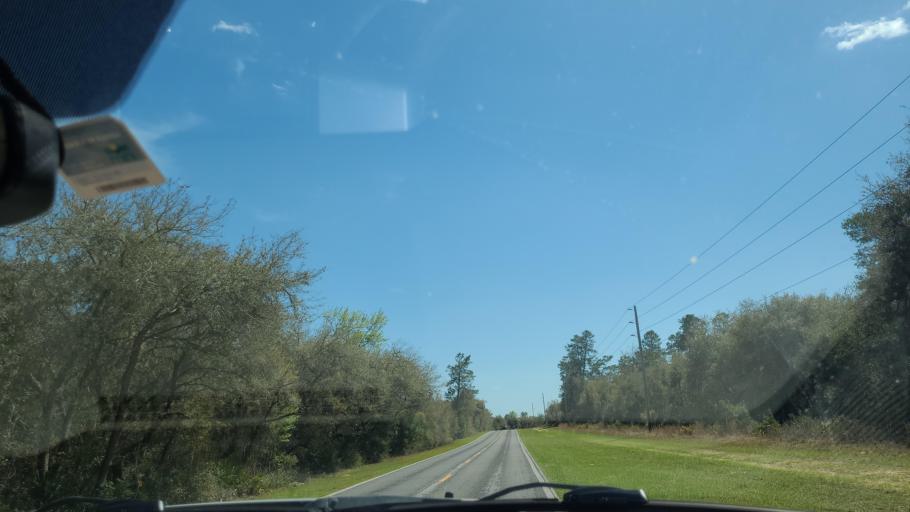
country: US
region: Florida
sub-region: Marion County
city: Citra
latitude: 29.4212
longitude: -81.9134
